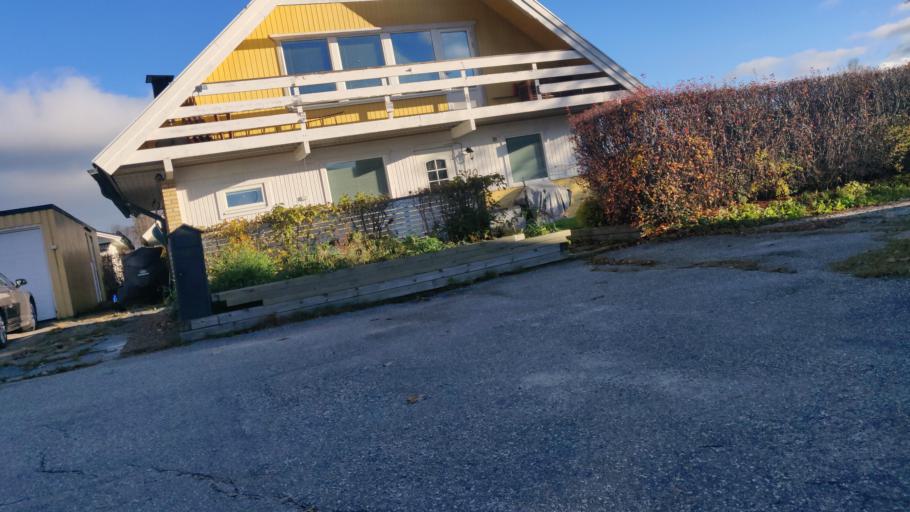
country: SE
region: Vaesternorrland
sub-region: Sundsvalls Kommun
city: Nolby
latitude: 62.2746
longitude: 17.3672
